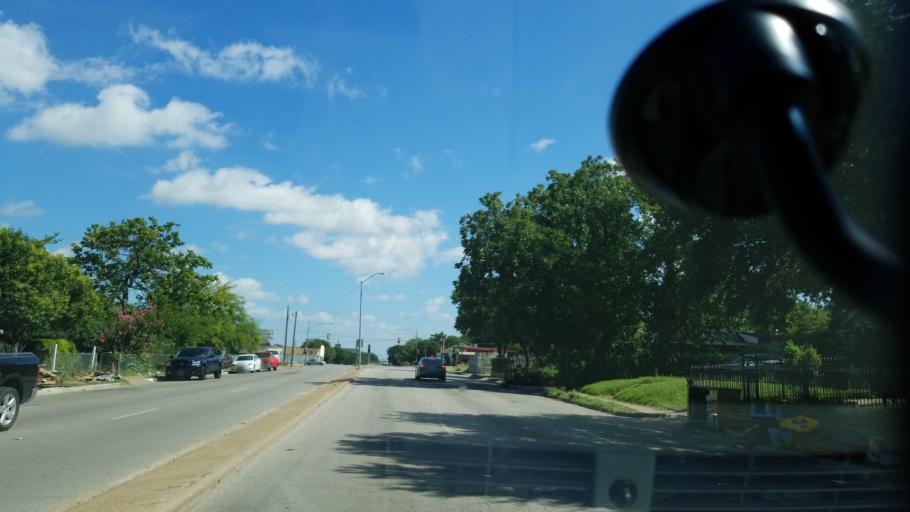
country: US
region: Texas
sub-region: Dallas County
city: Dallas
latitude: 32.7117
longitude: -96.8145
